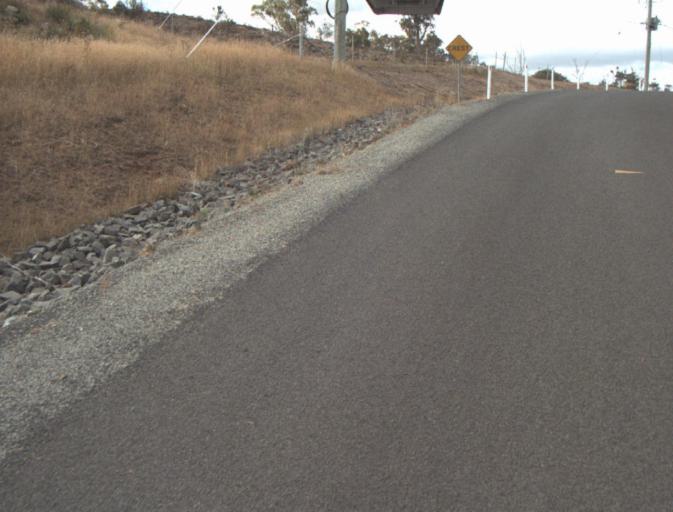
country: AU
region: Tasmania
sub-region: Launceston
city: Mayfield
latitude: -41.3002
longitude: 147.0447
